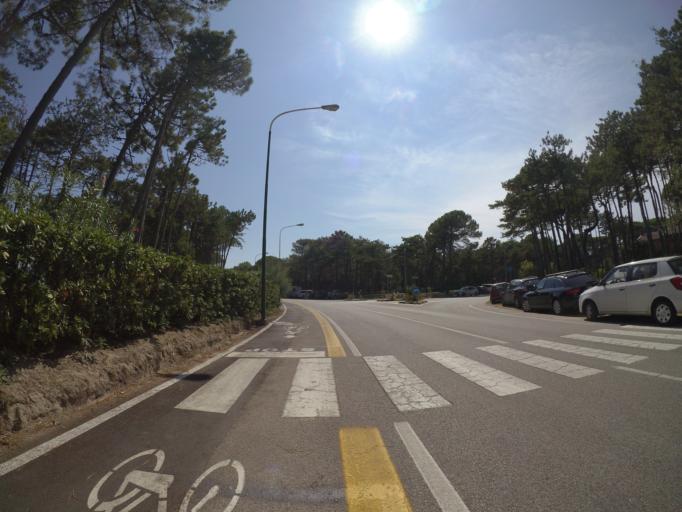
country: IT
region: Friuli Venezia Giulia
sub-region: Provincia di Udine
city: Lignano Sabbiadoro
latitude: 45.6575
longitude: 13.1037
